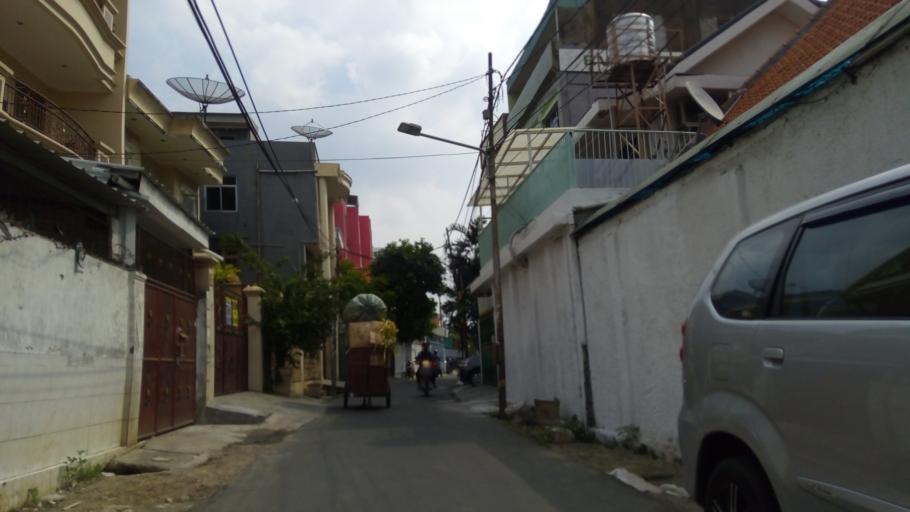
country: ID
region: Jakarta Raya
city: Jakarta
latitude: -6.1587
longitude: 106.8363
